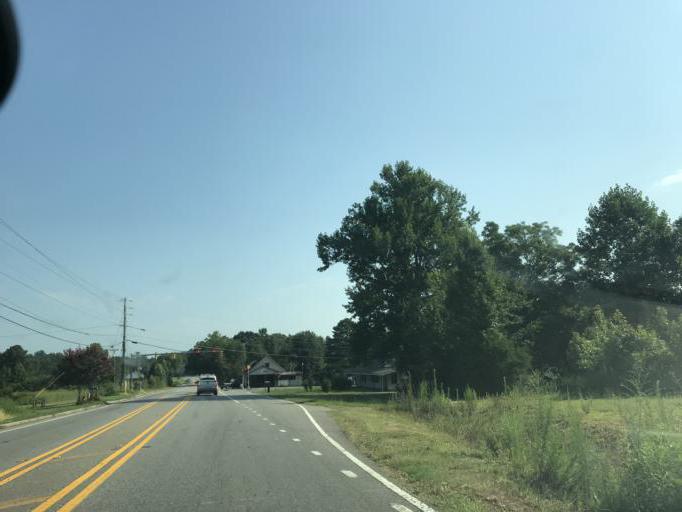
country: US
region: Georgia
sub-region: Forsyth County
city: Cumming
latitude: 34.2448
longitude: -84.1704
